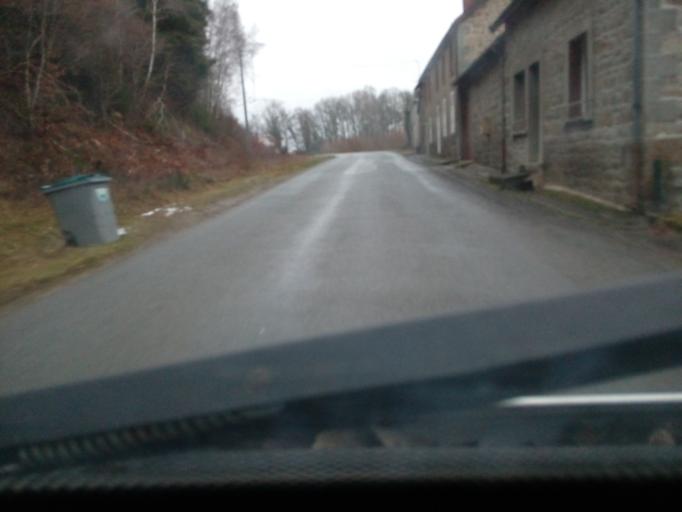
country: FR
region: Limousin
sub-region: Departement de la Creuse
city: Felletin
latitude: 45.8597
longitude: 2.2189
